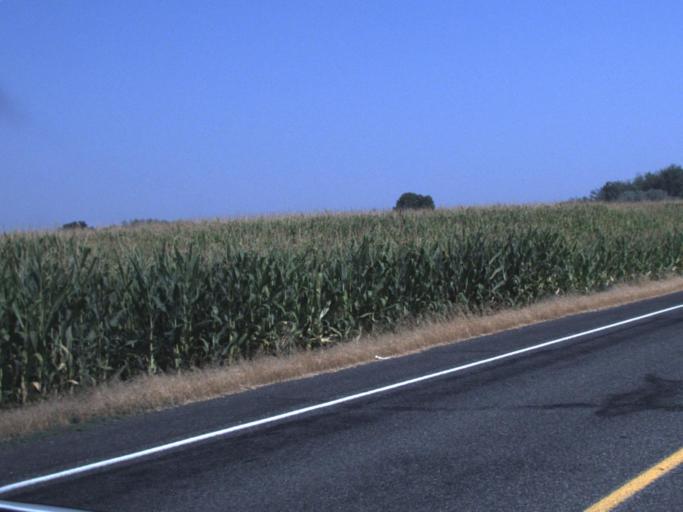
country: US
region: Washington
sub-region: Yakima County
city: Granger
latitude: 46.3249
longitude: -120.2381
